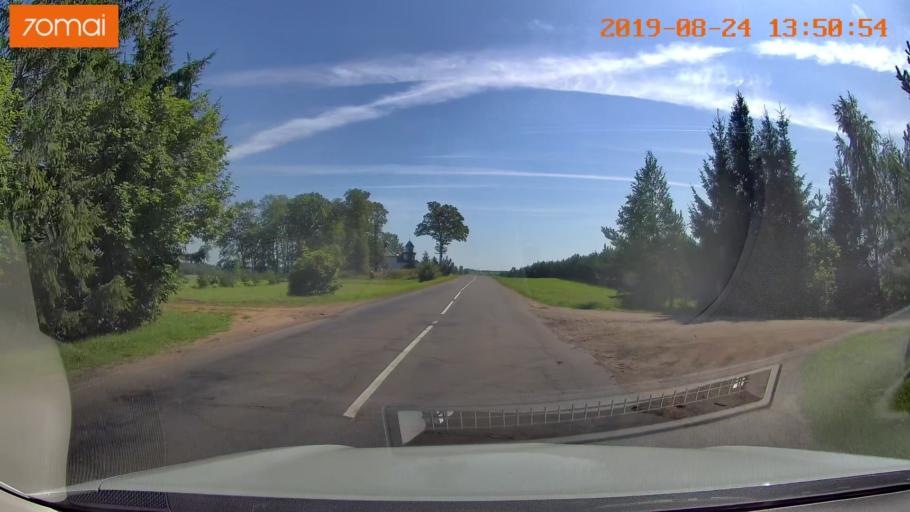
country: BY
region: Minsk
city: Samakhvalavichy
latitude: 53.6256
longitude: 27.5670
